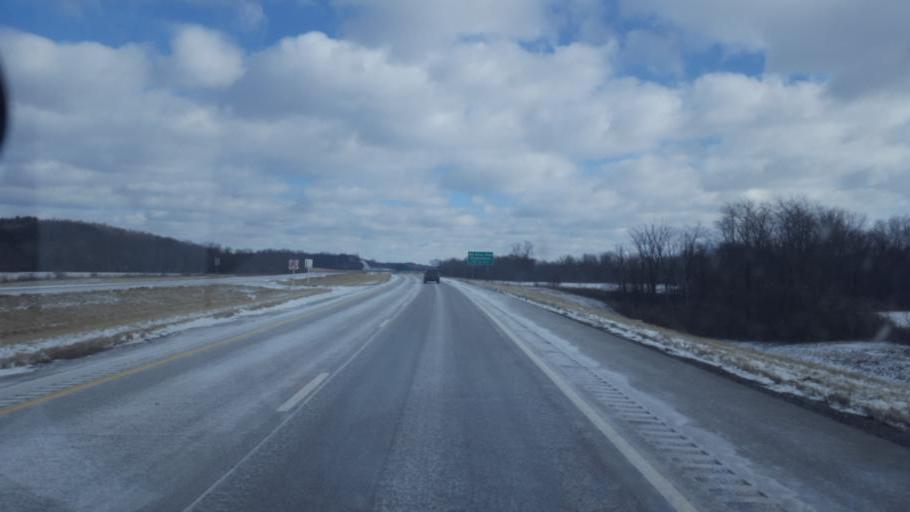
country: US
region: Ohio
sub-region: Muskingum County
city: Frazeysburg
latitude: 40.1302
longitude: -82.1114
